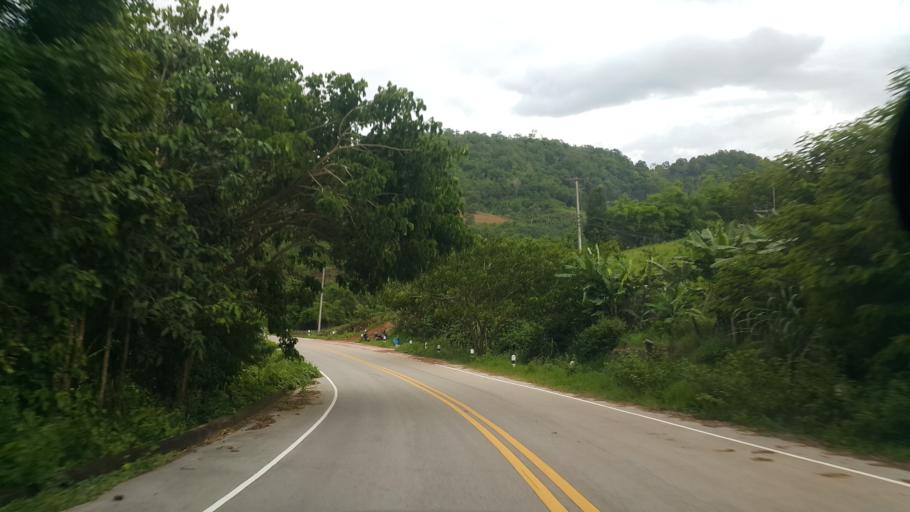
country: TH
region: Loei
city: Na Haeo
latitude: 17.4956
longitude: 101.0933
